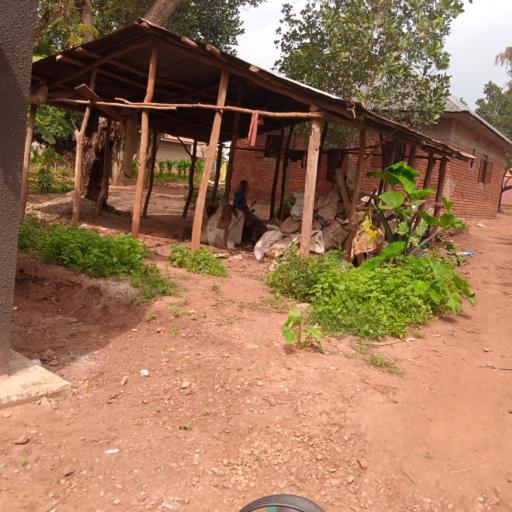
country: UG
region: Eastern Region
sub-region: Mbale District
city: Mbale
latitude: 1.1034
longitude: 34.1822
